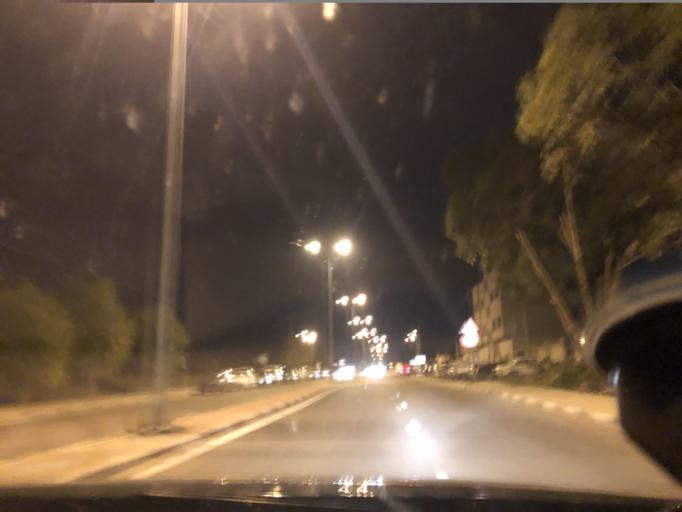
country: TN
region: Al Qasrayn
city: Kasserine
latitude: 35.1848
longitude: 8.8630
